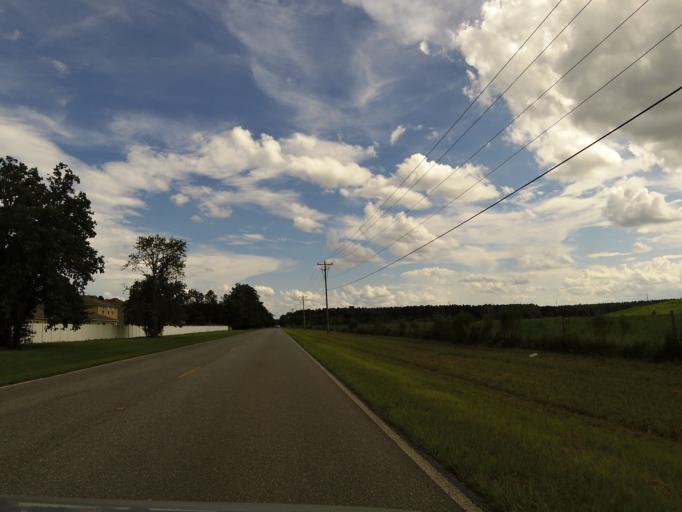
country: US
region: Florida
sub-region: Clay County
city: Green Cove Springs
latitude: 30.0041
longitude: -81.7315
